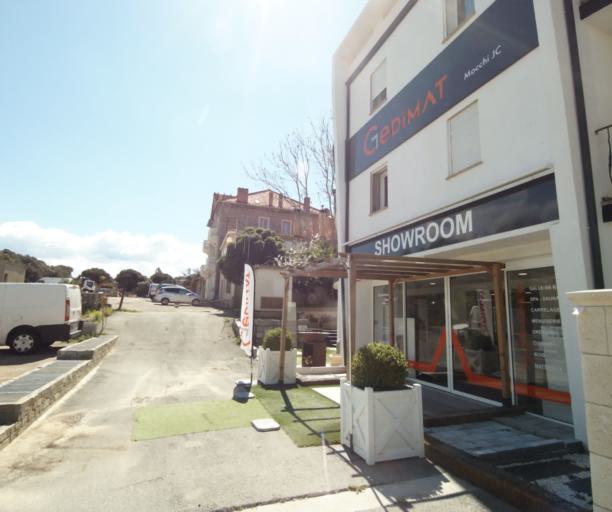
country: FR
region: Corsica
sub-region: Departement de la Corse-du-Sud
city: Propriano
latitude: 41.6735
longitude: 8.9062
